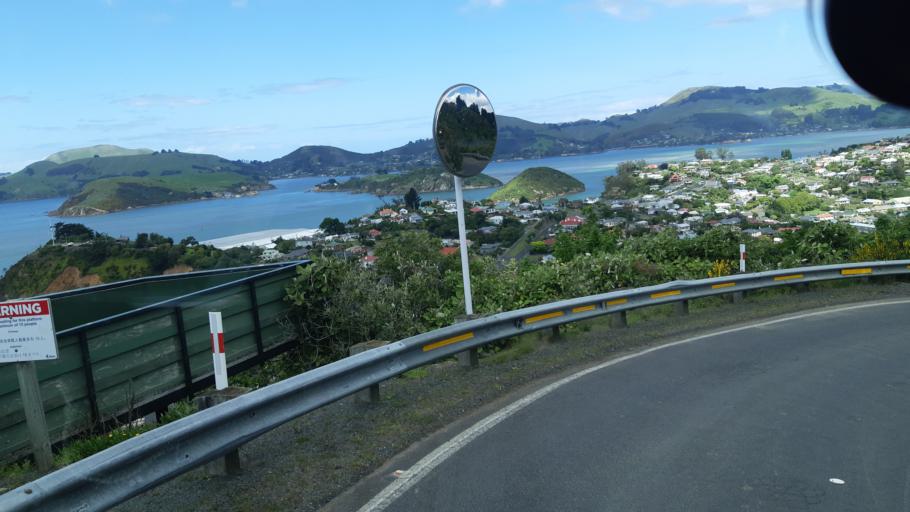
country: NZ
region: Otago
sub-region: Dunedin City
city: Portobello
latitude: -45.8121
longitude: 170.6197
